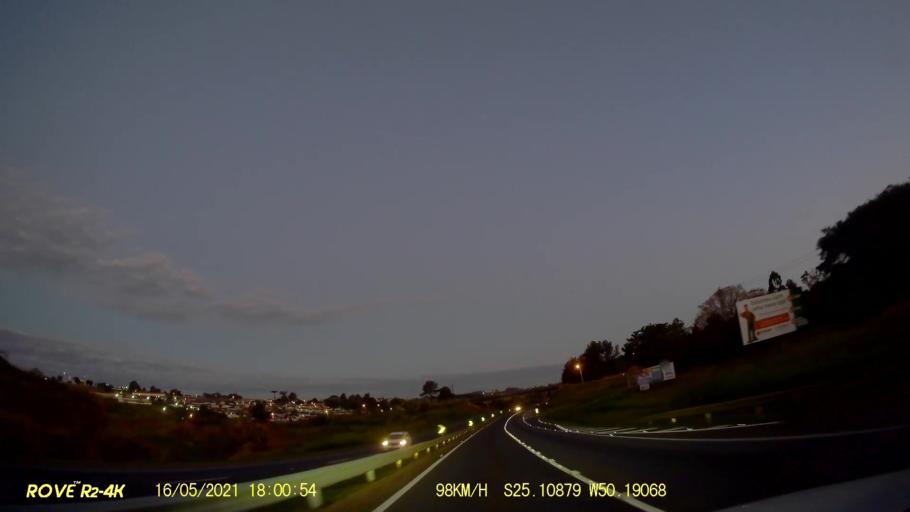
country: BR
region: Parana
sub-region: Ponta Grossa
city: Ponta Grossa
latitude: -25.1087
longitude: -50.1910
